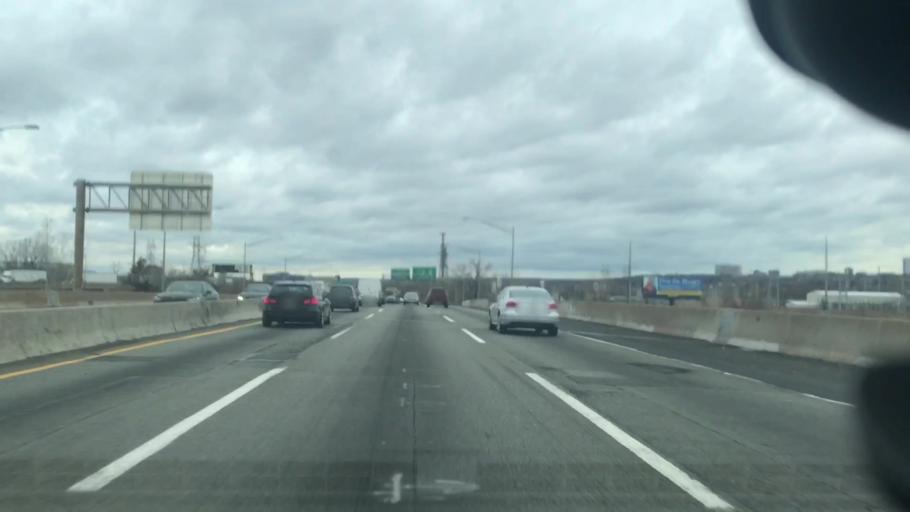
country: US
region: New Jersey
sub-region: Bergen County
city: Ridgefield
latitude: 40.8297
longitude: -74.0241
